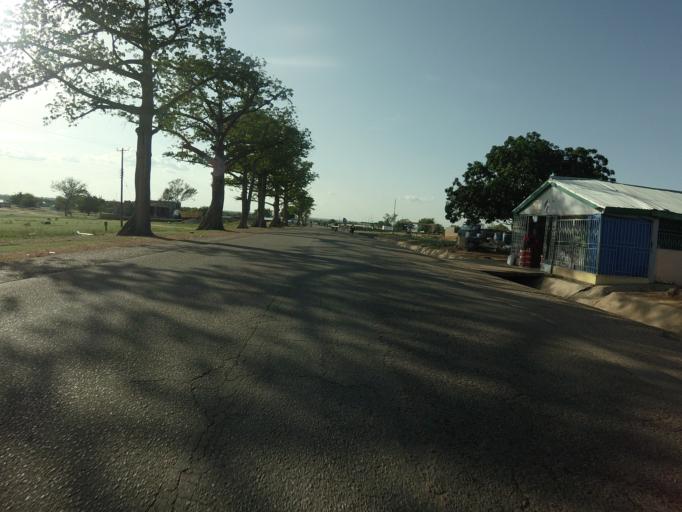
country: GH
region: Upper East
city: Navrongo
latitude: 10.9809
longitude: -1.1063
